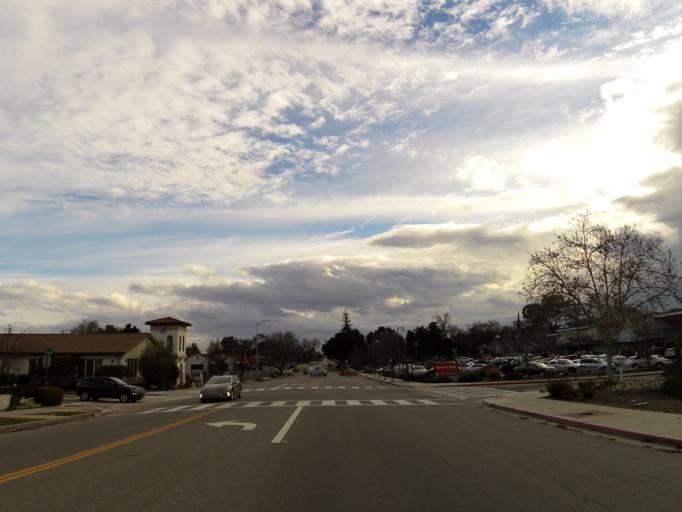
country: US
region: California
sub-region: San Luis Obispo County
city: Paso Robles
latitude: 35.6375
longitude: -120.6923
